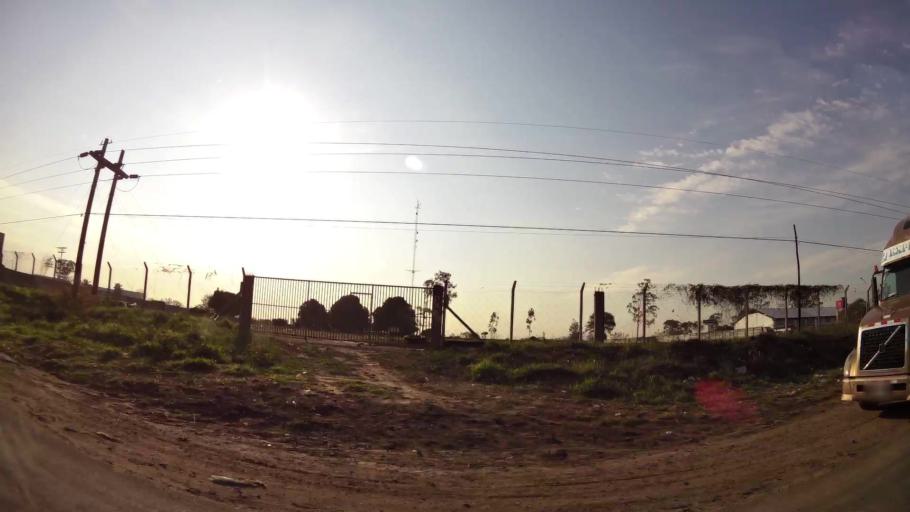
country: BO
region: Santa Cruz
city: Santa Cruz de la Sierra
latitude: -17.6826
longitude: -63.1589
